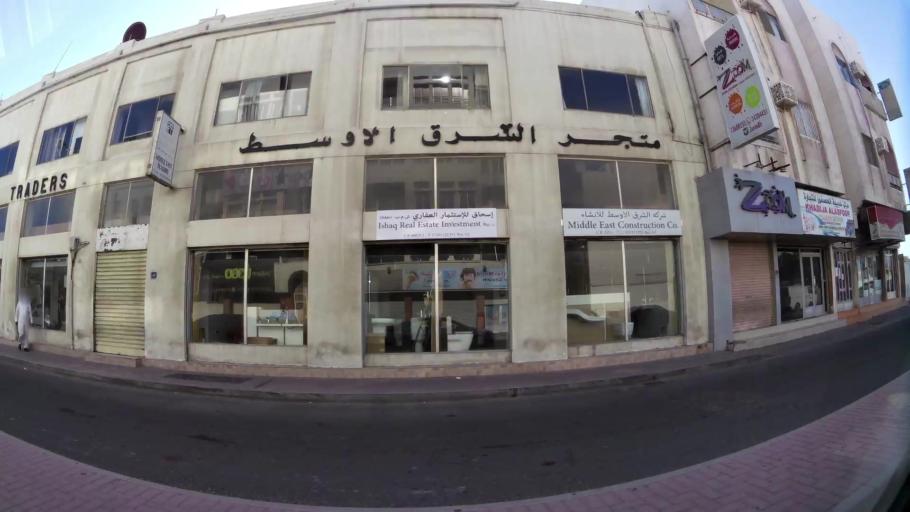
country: BH
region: Manama
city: Manama
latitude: 26.2357
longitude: 50.5828
